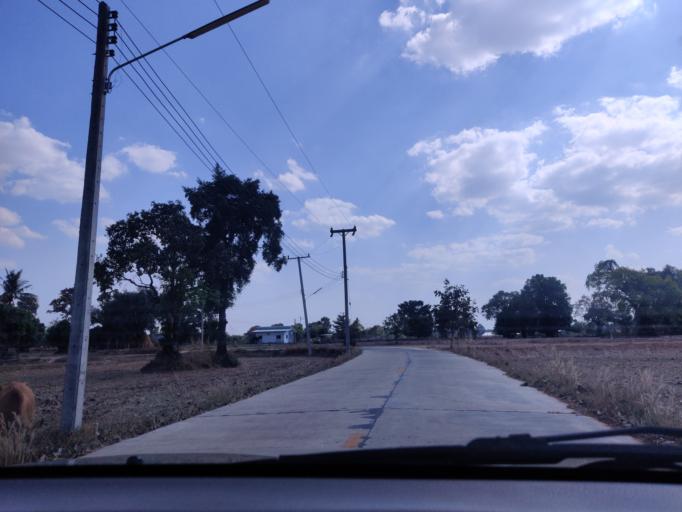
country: TH
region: Sisaket
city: Si Sa Ket
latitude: 15.0879
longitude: 104.3531
